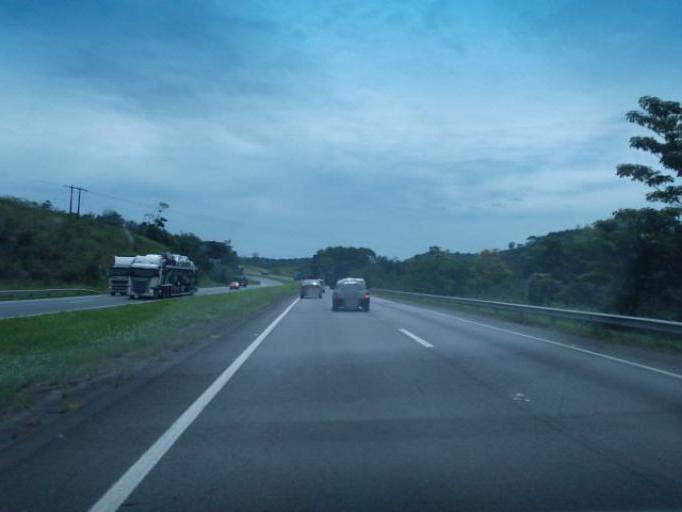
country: BR
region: Sao Paulo
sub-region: Miracatu
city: Miracatu
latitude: -24.2925
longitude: -47.4735
